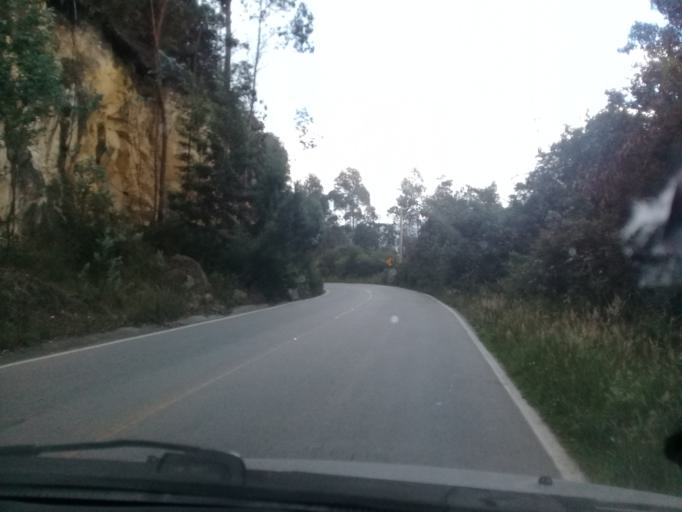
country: CO
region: Cundinamarca
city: Tabio
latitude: 4.9348
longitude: -74.1130
